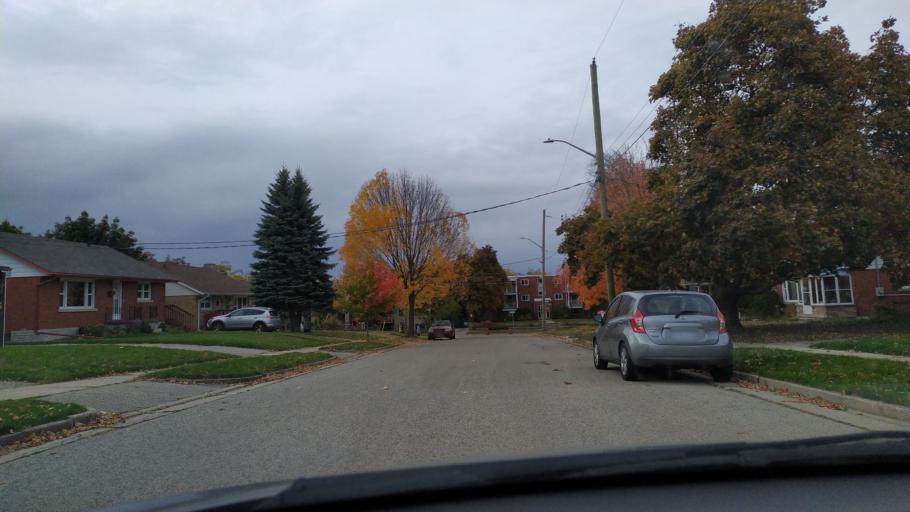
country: CA
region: Ontario
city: Waterloo
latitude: 43.4674
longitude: -80.5122
